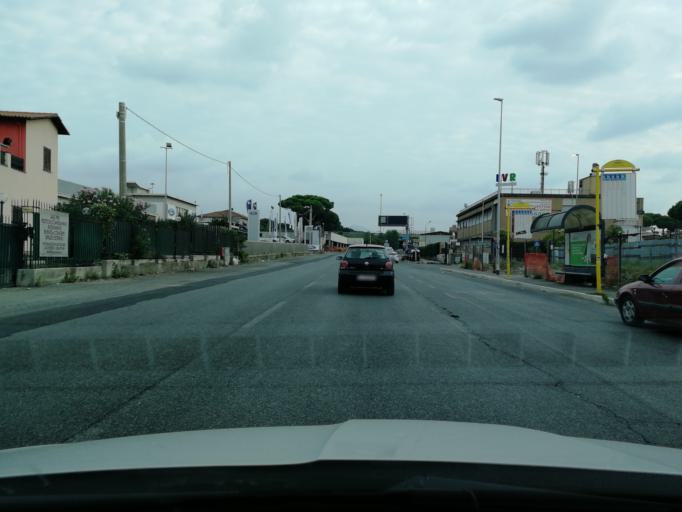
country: IT
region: Latium
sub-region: Citta metropolitana di Roma Capitale
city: Ciampino
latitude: 41.8397
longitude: 12.5882
